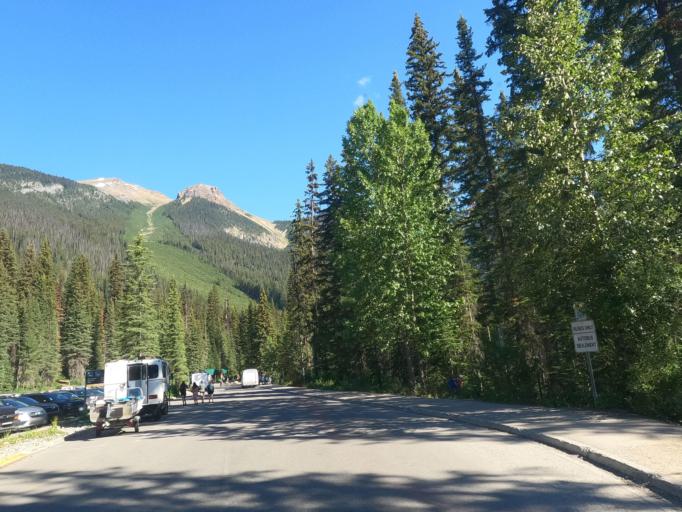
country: CA
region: Alberta
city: Lake Louise
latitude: 51.4384
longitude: -116.5405
